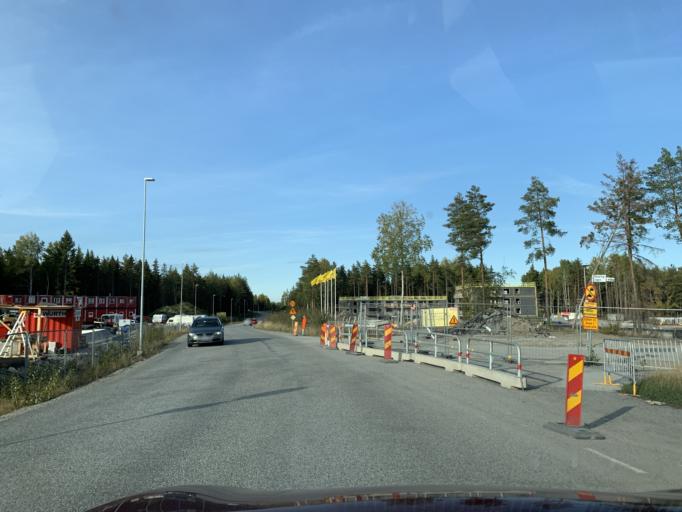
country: SE
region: Stockholm
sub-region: Upplands-Bro Kommun
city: Bro
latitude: 59.5060
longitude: 17.6148
